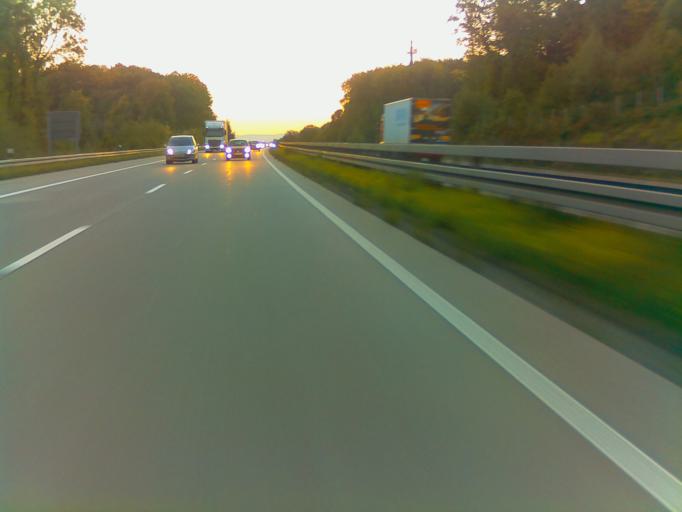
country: DE
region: Hesse
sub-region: Regierungsbezirk Giessen
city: Lich
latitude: 50.5151
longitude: 8.7517
